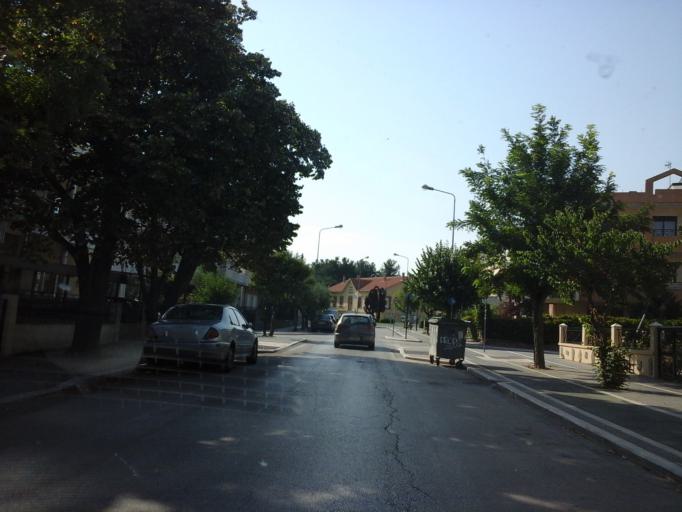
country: GR
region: East Macedonia and Thrace
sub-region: Nomos Evrou
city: Alexandroupoli
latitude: 40.8522
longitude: 25.8711
